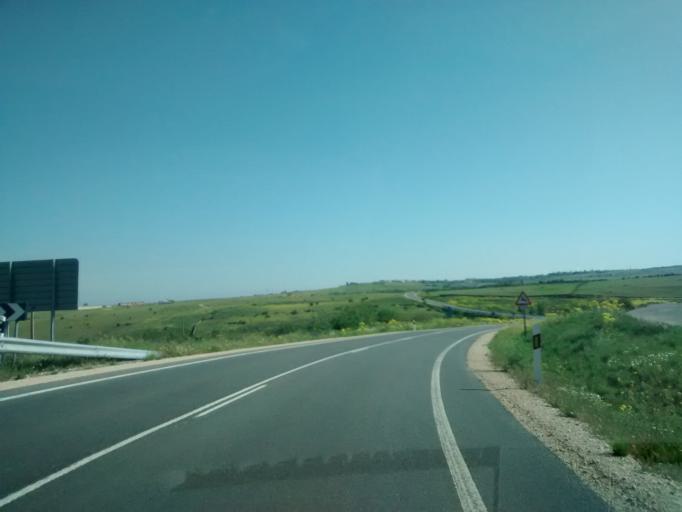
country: ES
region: Castille and Leon
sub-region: Provincia de Segovia
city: Trescasas
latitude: 40.9653
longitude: -4.0337
